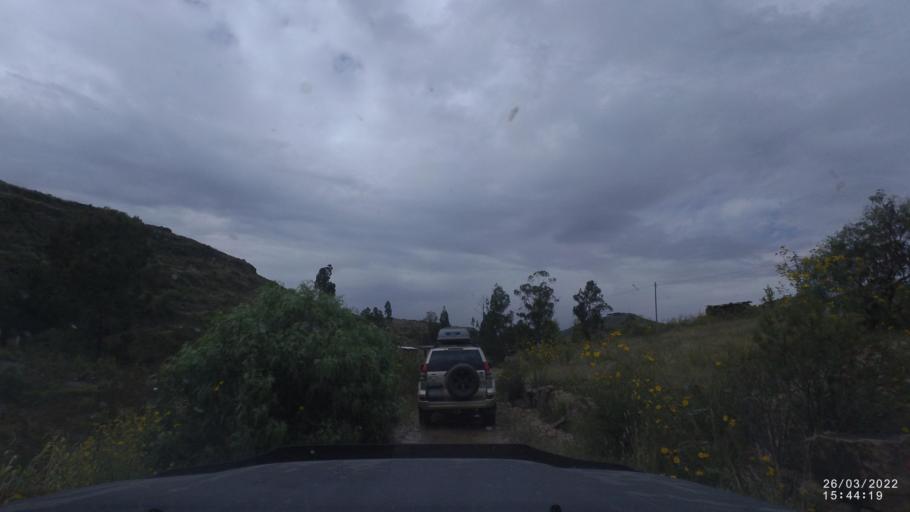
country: BO
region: Cochabamba
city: Cliza
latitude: -17.7488
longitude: -65.8595
